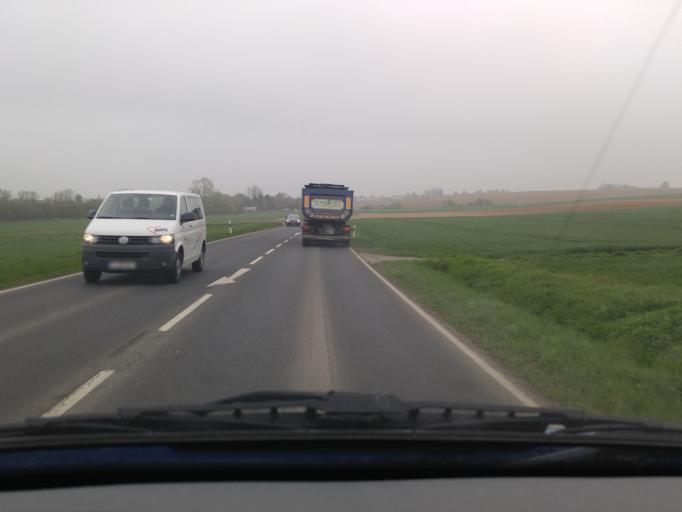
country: DE
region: Hesse
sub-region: Regierungsbezirk Darmstadt
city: Karben
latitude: 50.2684
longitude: 8.7573
